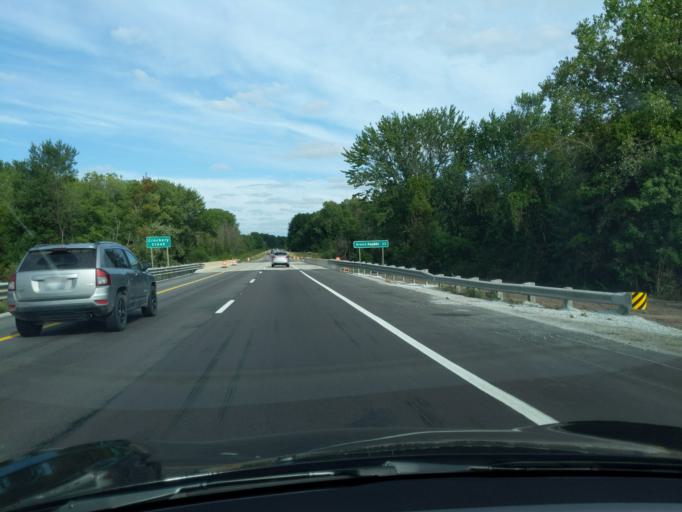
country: US
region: Michigan
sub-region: Muskegon County
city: Fruitport
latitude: 43.0737
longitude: -86.0534
